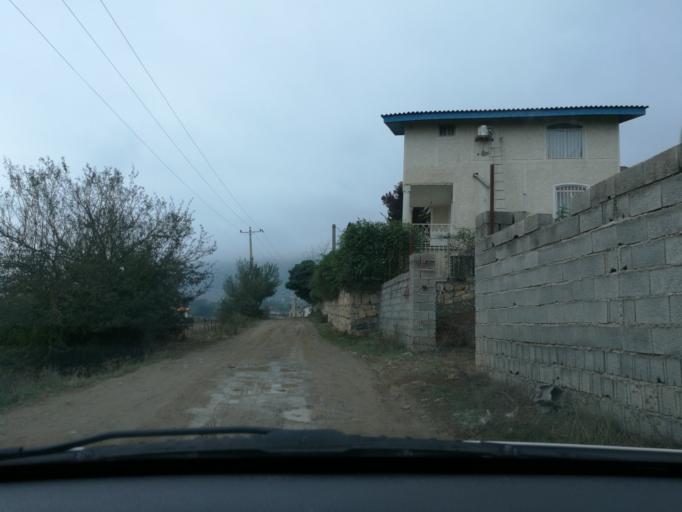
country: IR
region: Mazandaran
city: `Abbasabad
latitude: 36.5031
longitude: 51.2048
